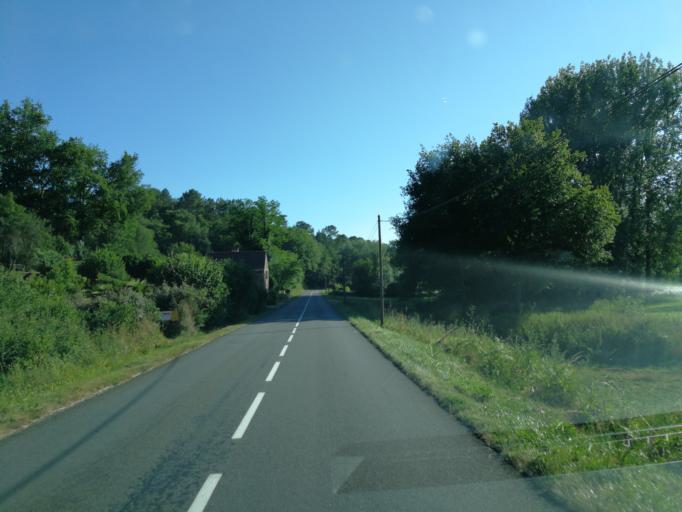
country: FR
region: Midi-Pyrenees
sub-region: Departement du Lot
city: Prayssac
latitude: 44.5964
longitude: 1.1794
